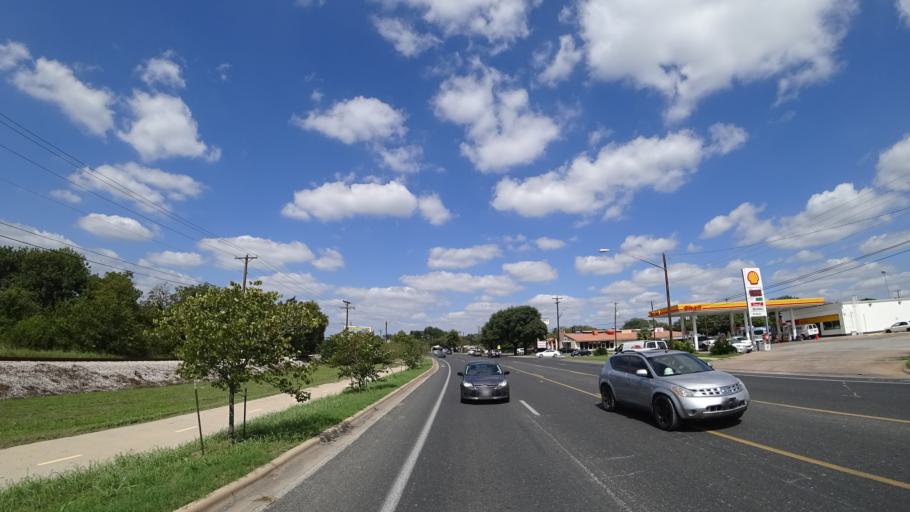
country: US
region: Texas
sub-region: Travis County
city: Austin
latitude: 30.3298
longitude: -97.7157
